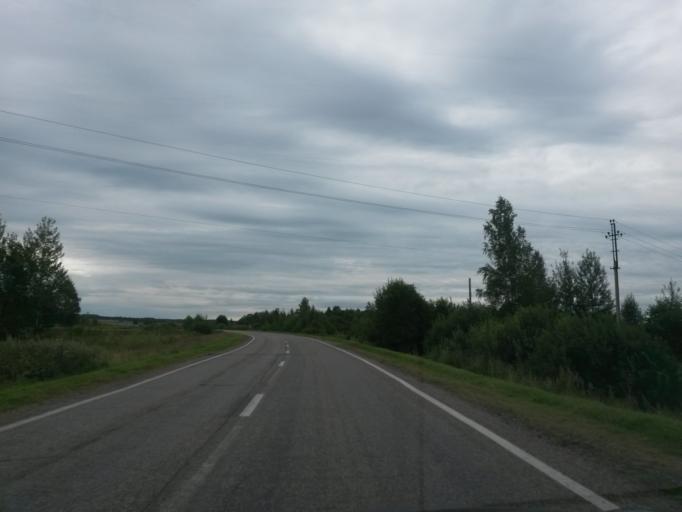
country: RU
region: Jaroslavl
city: Gavrilov-Yam
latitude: 57.3187
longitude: 39.8709
